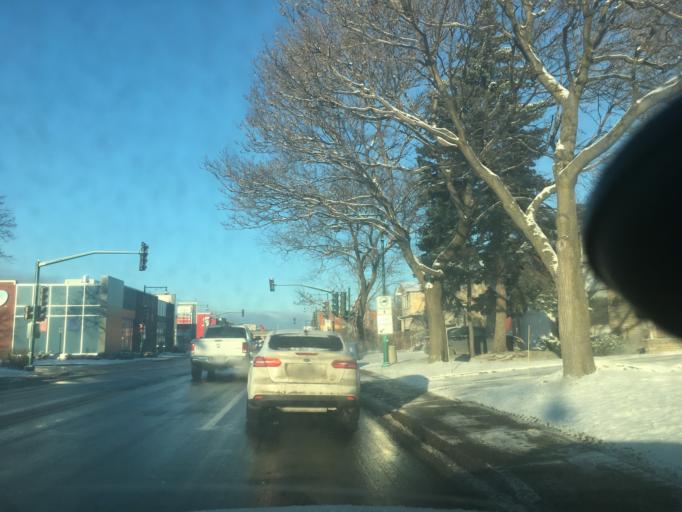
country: CA
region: Quebec
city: Saint-Laurent
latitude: 45.5069
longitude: -73.6595
